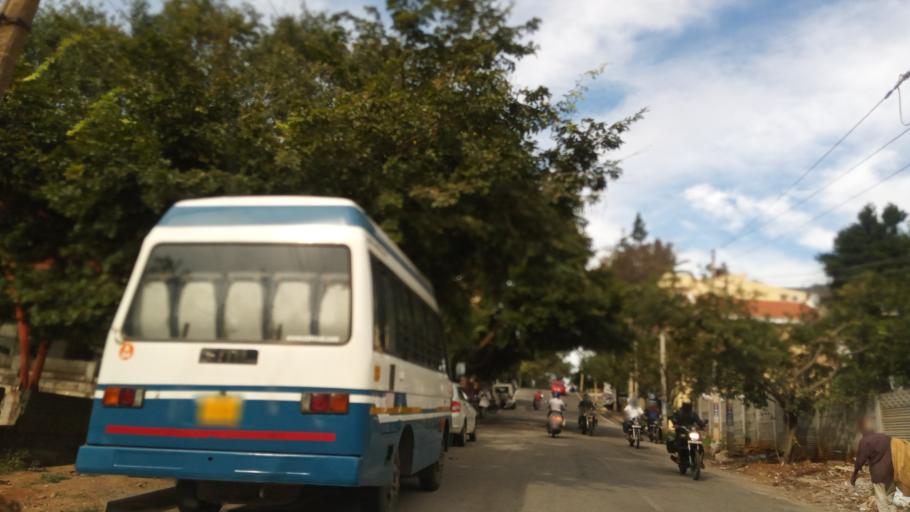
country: IN
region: Karnataka
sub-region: Bangalore Urban
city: Bangalore
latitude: 13.0104
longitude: 77.5482
